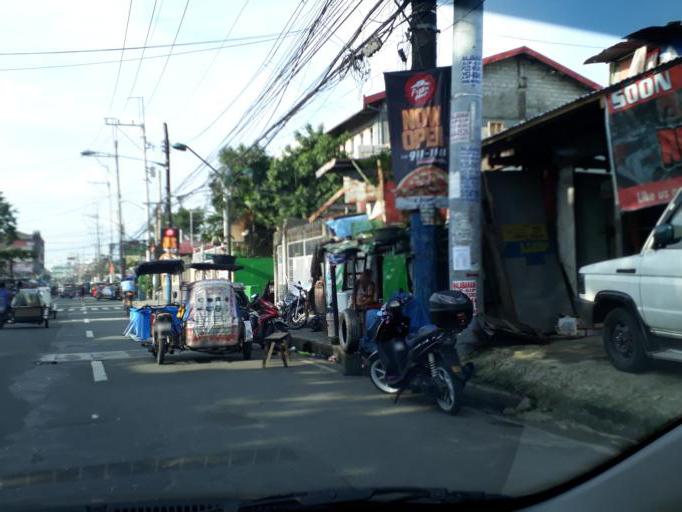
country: PH
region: Metro Manila
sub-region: City of Manila
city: Manila
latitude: 14.6332
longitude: 120.9749
